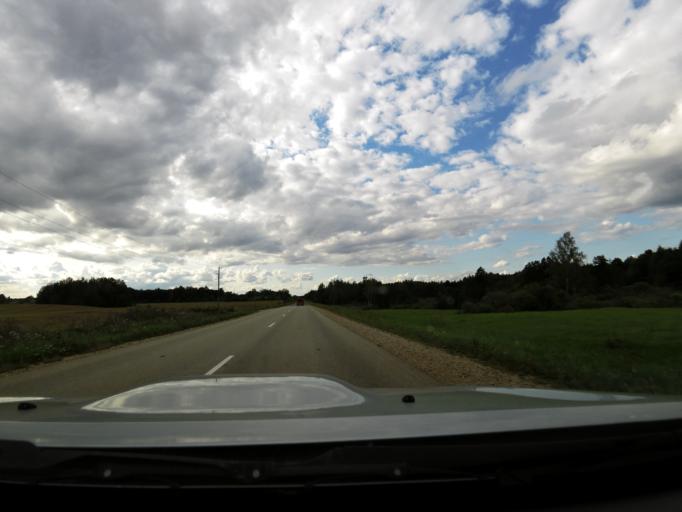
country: LV
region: Akniste
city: Akniste
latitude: 55.9903
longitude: 25.9787
